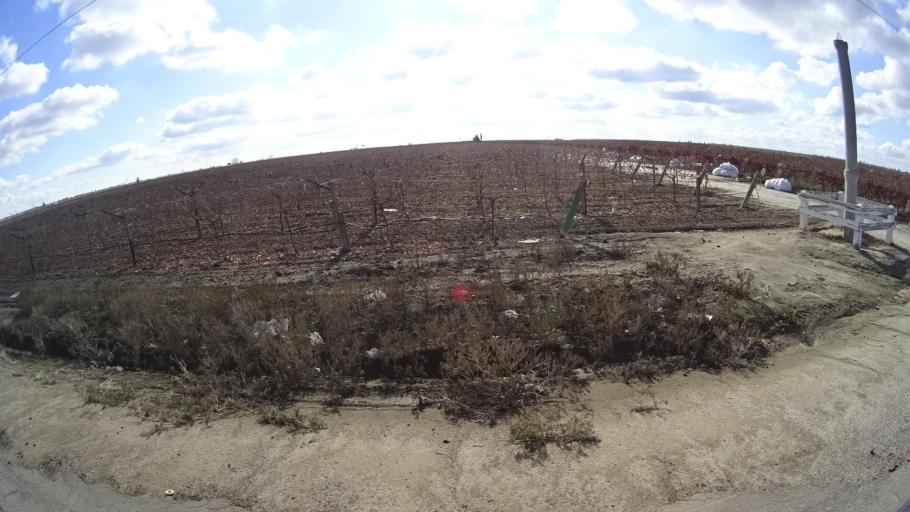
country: US
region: California
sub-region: Kern County
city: McFarland
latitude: 35.6888
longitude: -119.2542
